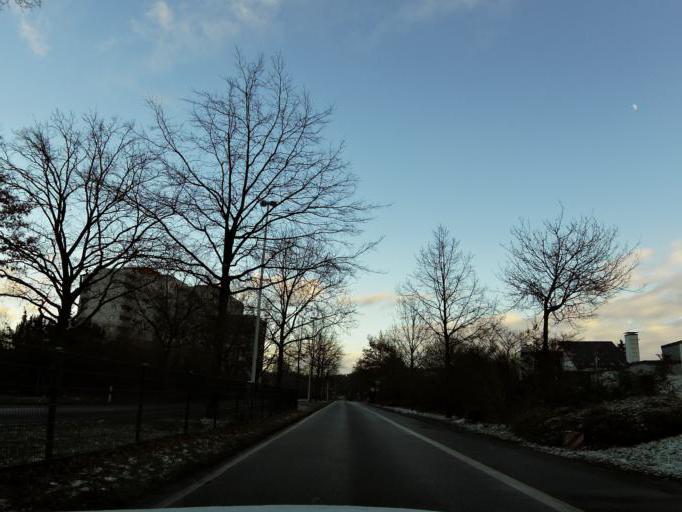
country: DE
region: Hesse
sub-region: Regierungsbezirk Darmstadt
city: Darmstadt
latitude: 49.8956
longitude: 8.6841
